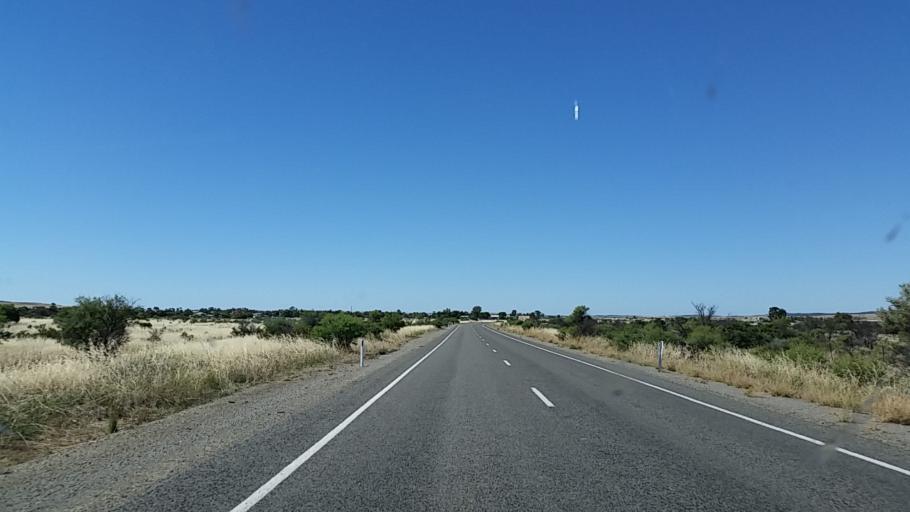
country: AU
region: South Australia
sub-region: Peterborough
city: Peterborough
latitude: -33.1619
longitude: 138.9172
